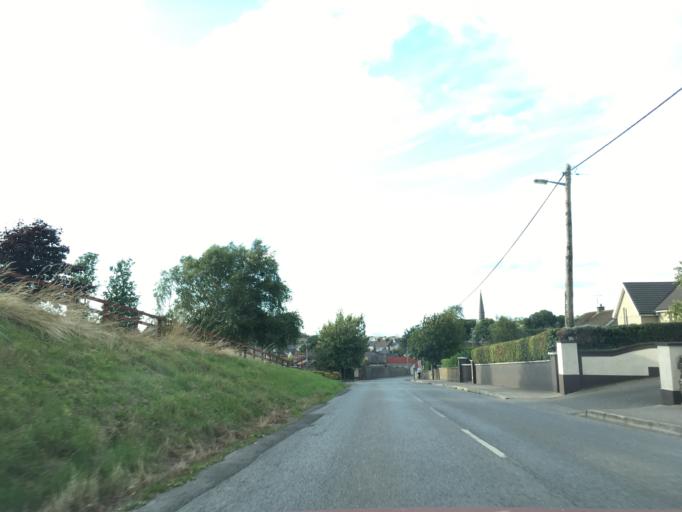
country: IE
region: Munster
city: Cashel
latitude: 52.5121
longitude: -7.8859
